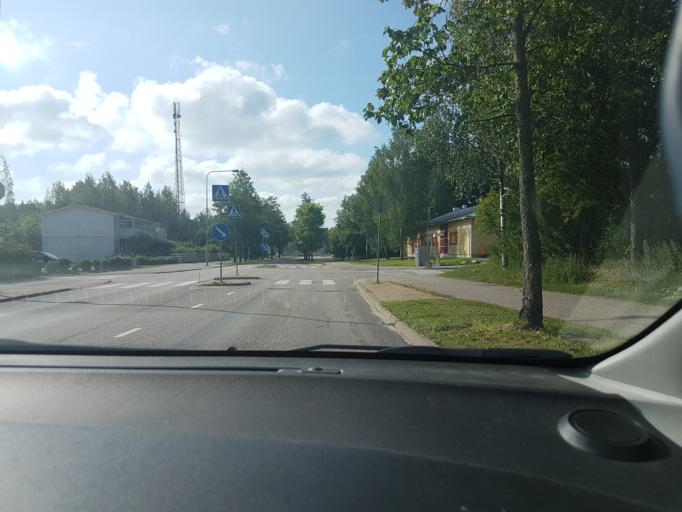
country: FI
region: Uusimaa
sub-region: Helsinki
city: Vantaa
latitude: 60.3261
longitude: 25.0248
